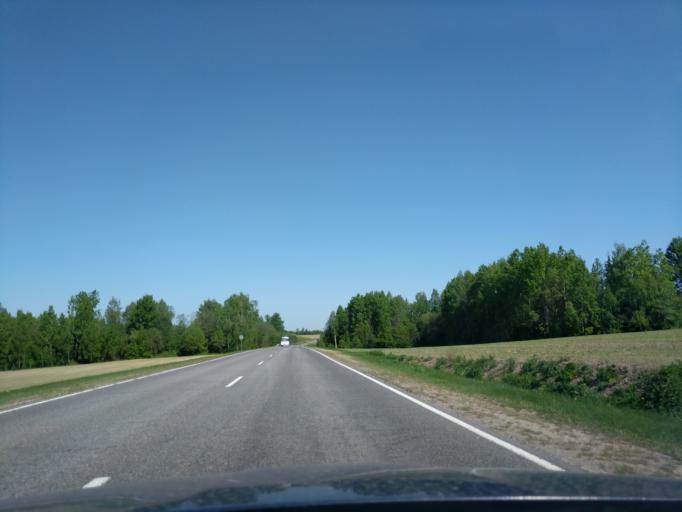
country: BY
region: Minsk
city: Il'ya
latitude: 54.3039
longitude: 27.4753
